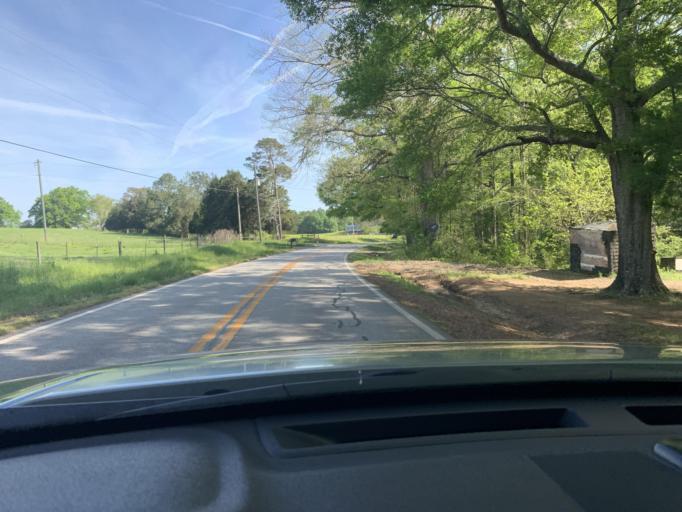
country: US
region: Georgia
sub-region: Oconee County
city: Watkinsville
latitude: 33.8022
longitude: -83.3190
